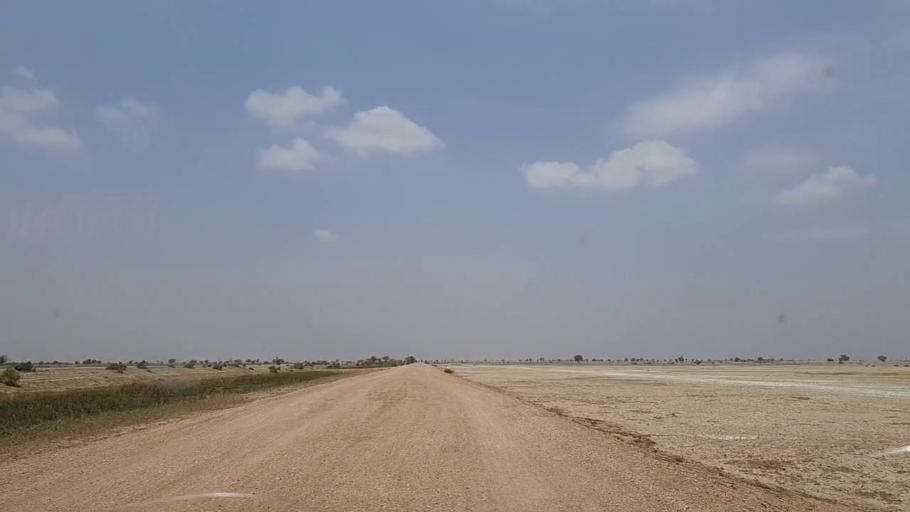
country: PK
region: Sindh
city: Johi
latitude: 26.7609
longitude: 67.6640
